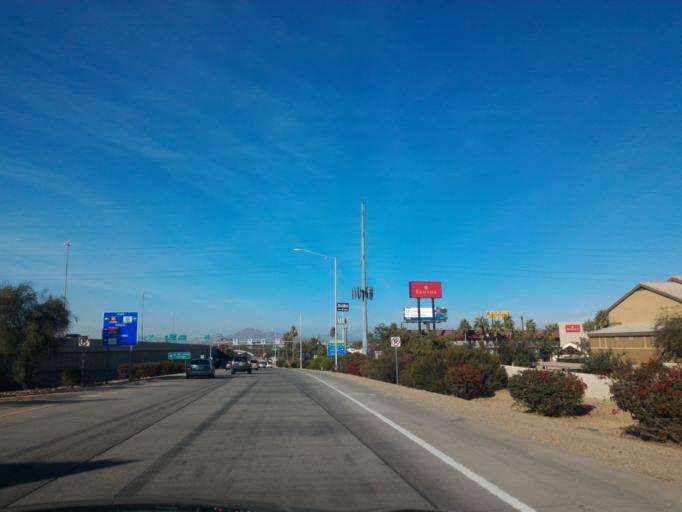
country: US
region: Arizona
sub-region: Maricopa County
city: Guadalupe
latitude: 33.3758
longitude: -111.9674
